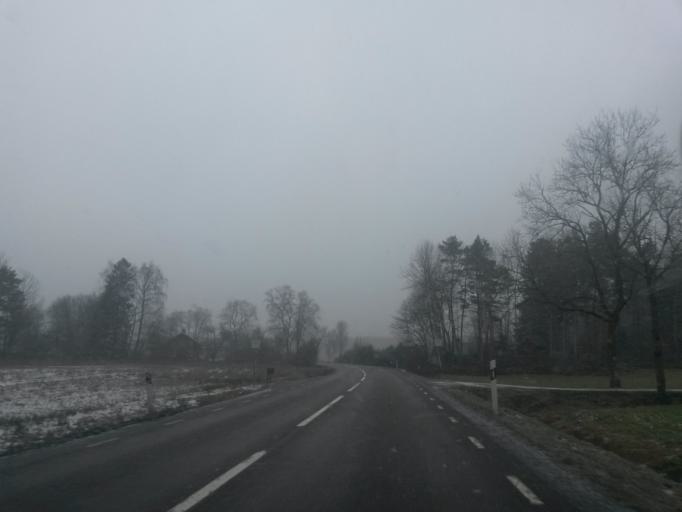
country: SE
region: Vaestra Goetaland
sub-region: Vanersborgs Kommun
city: Vargon
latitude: 58.2261
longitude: 12.4243
